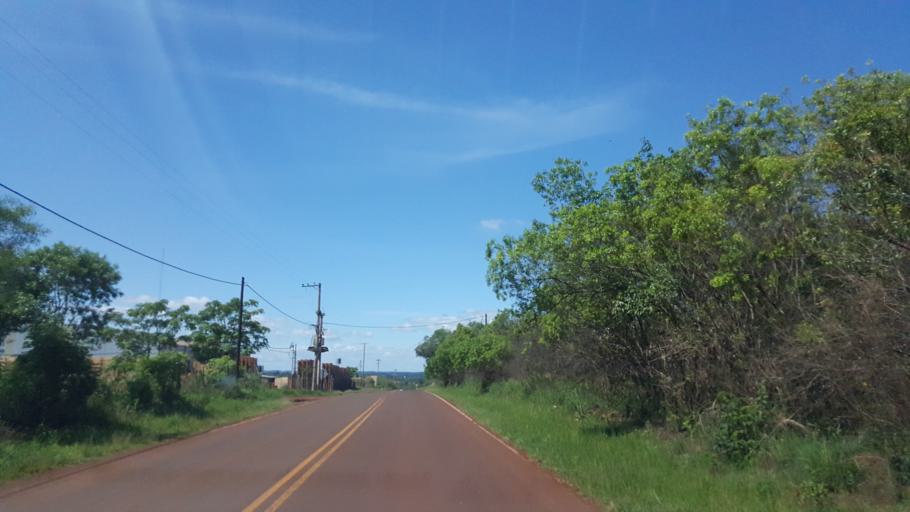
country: AR
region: Misiones
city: Garupa
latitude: -27.5008
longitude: -55.8479
